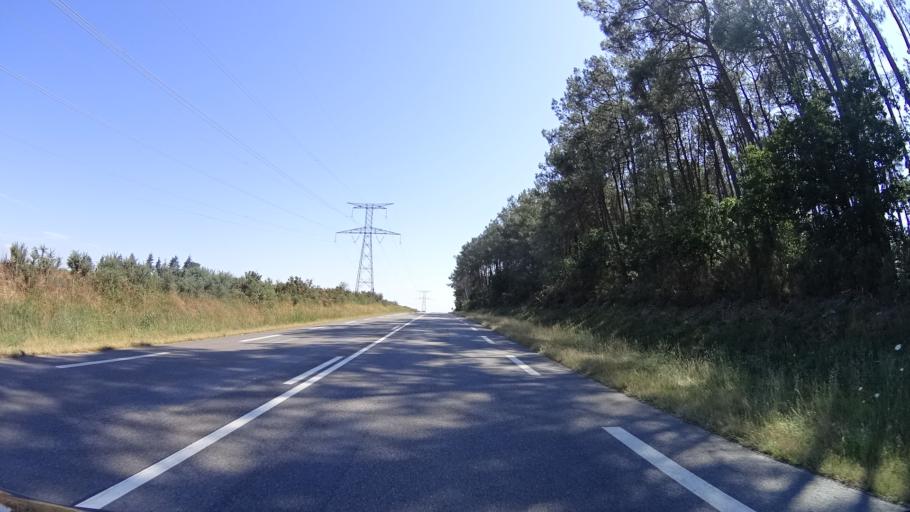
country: FR
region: Brittany
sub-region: Departement du Morbihan
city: Saint-Dolay
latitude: 47.5589
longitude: -2.1334
